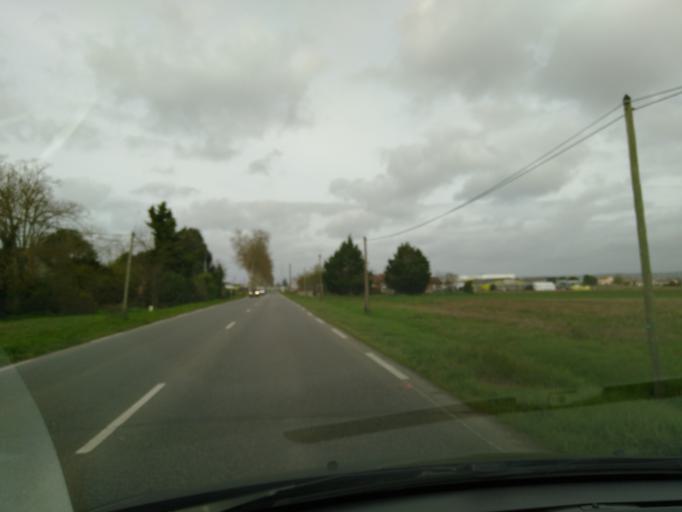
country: FR
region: Midi-Pyrenees
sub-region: Departement de la Haute-Garonne
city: Grenade
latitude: 43.7524
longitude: 1.3042
